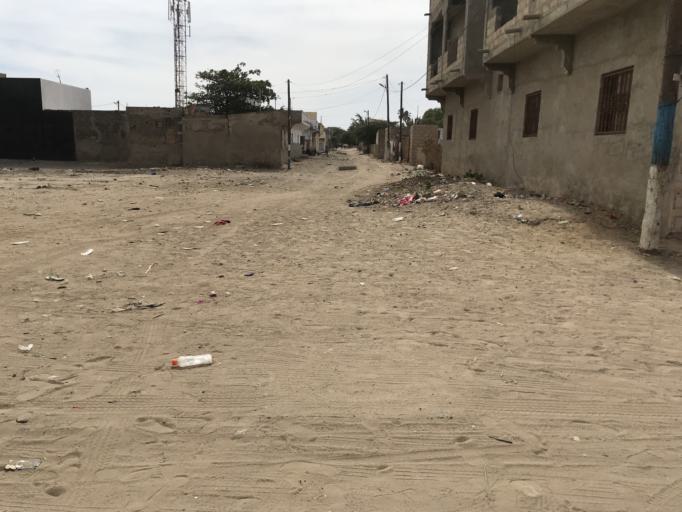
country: SN
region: Saint-Louis
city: Saint-Louis
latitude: 16.0249
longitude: -16.4836
